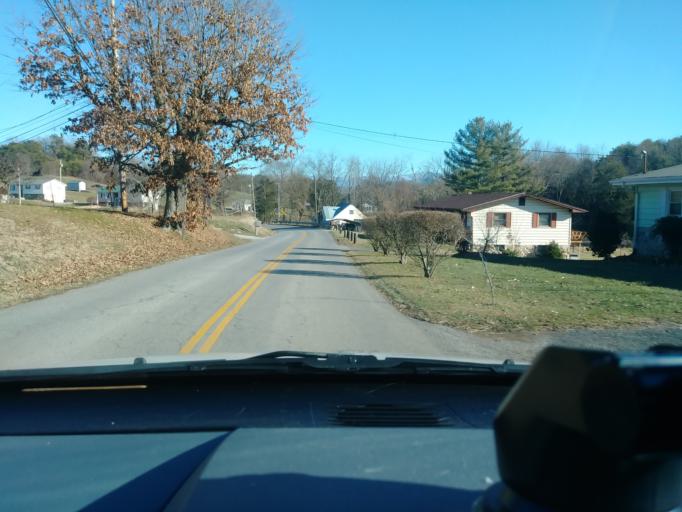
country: US
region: Tennessee
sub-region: Greene County
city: Greeneville
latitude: 36.1126
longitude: -82.8733
